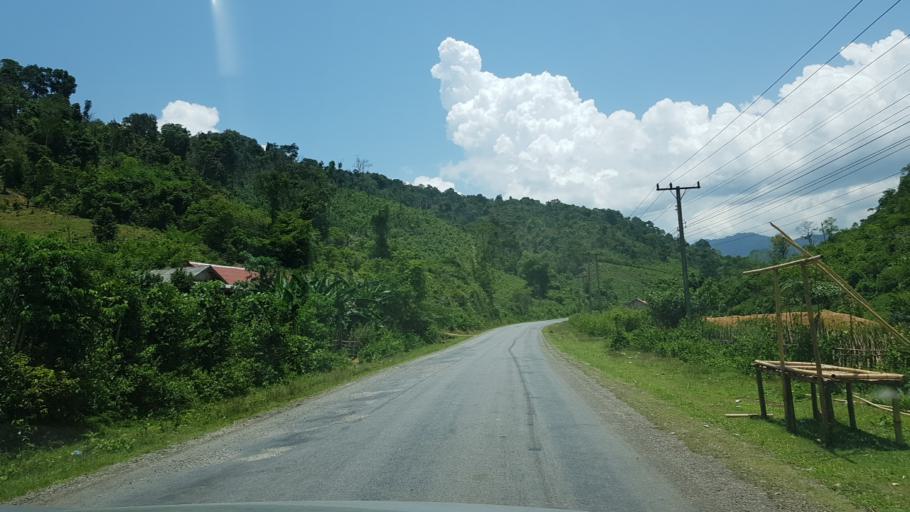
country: LA
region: Vientiane
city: Muang Kasi
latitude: 19.1317
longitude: 102.2304
